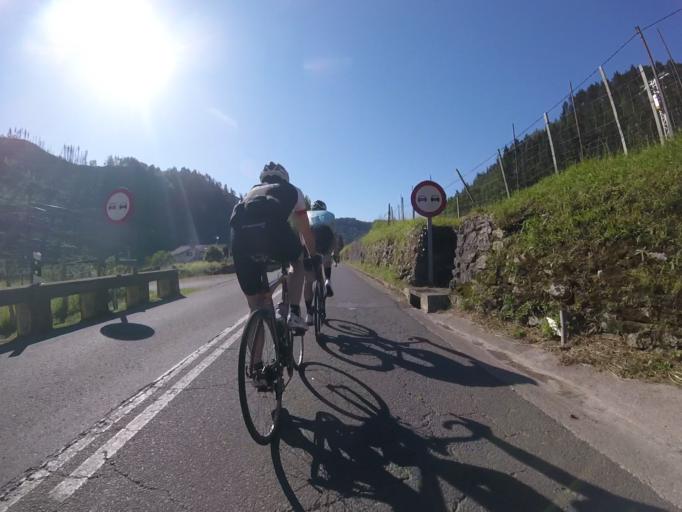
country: ES
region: Basque Country
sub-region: Provincia de Guipuzcoa
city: Azpeitia
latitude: 43.1521
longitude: -2.2400
